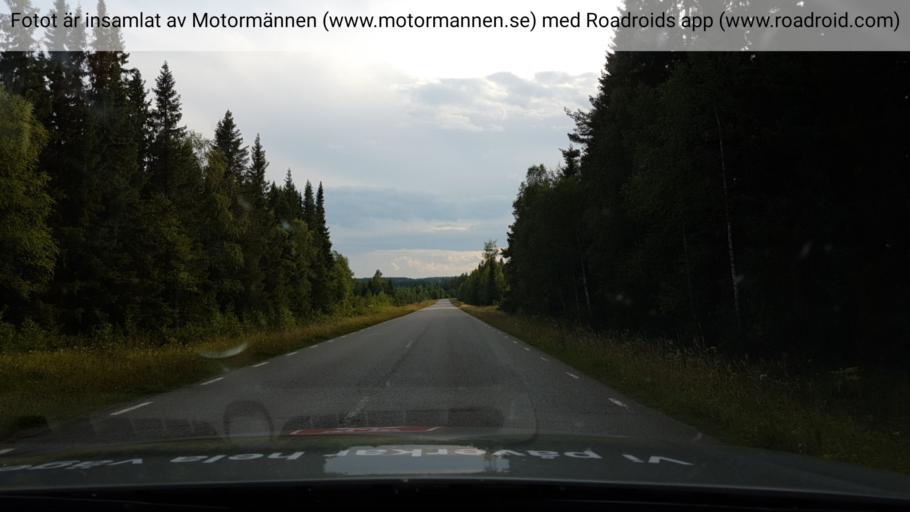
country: SE
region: Jaemtland
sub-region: Stroemsunds Kommun
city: Stroemsund
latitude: 63.5486
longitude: 15.3820
